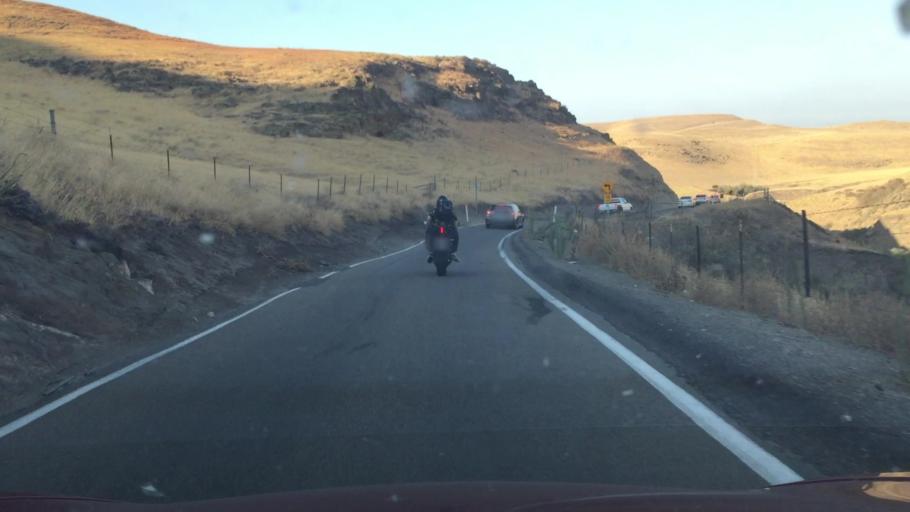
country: US
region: California
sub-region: San Joaquin County
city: Mountain House
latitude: 37.6907
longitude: -121.5940
